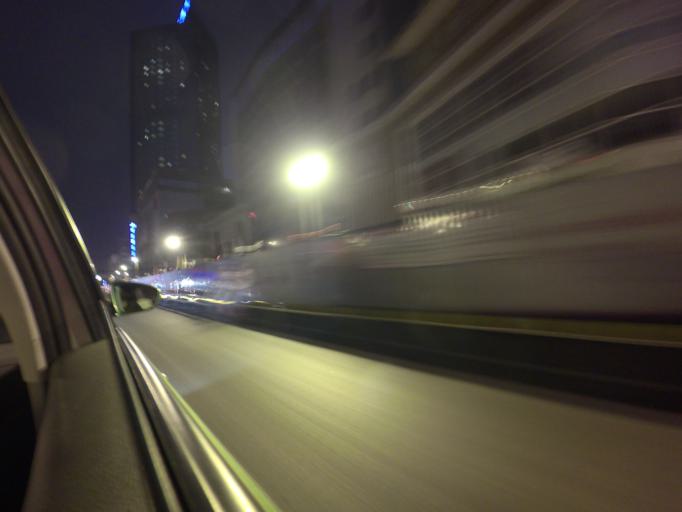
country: CN
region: Sichuan
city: Chengdu
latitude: 30.6697
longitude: 104.0661
